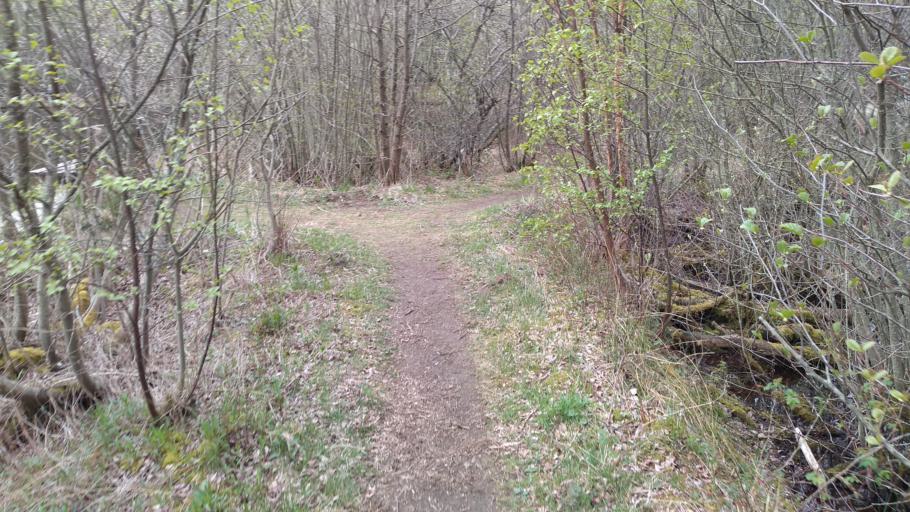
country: GB
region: Scotland
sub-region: Perth and Kinross
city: Aberfeldy
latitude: 56.7055
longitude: -4.0030
